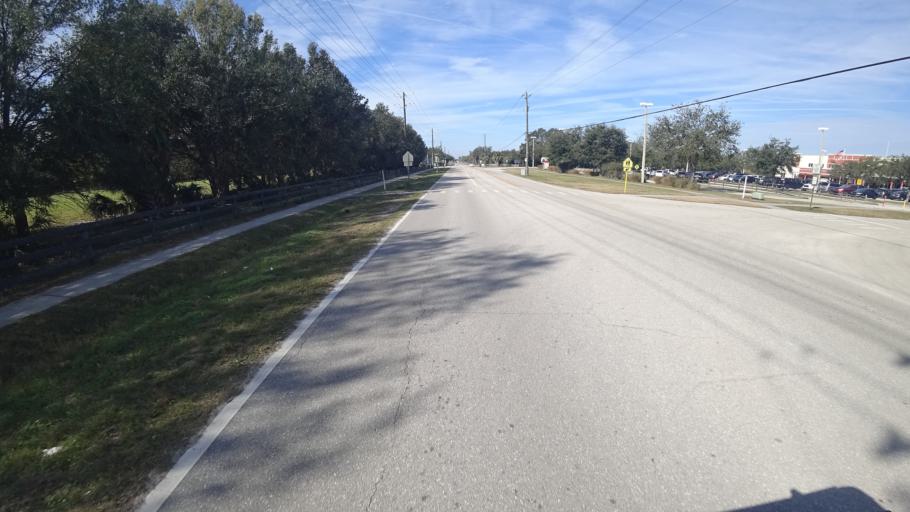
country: US
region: Florida
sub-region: Manatee County
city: Ellenton
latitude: 27.5739
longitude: -82.4897
